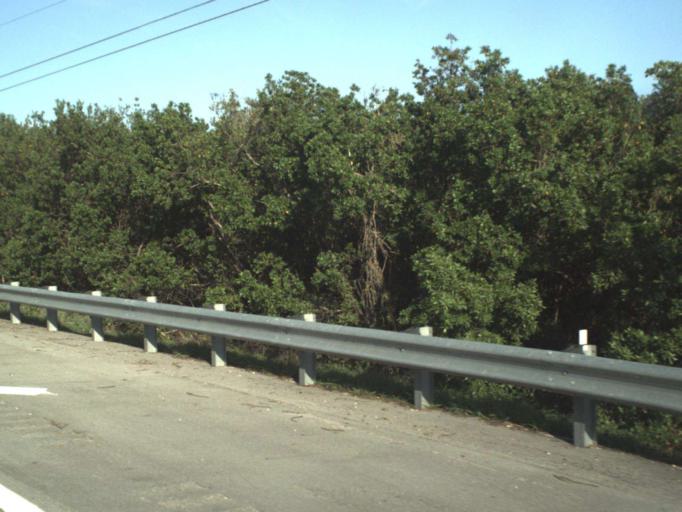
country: US
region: Florida
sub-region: Monroe County
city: Marathon
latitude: 24.7735
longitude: -80.9333
